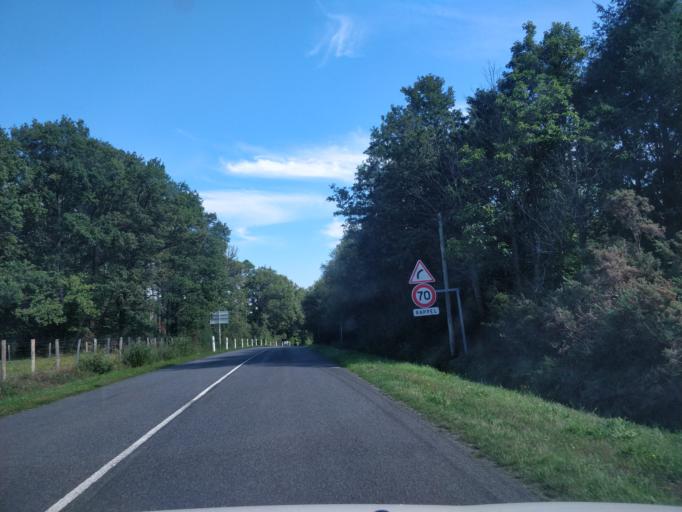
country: FR
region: Pays de la Loire
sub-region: Departement de la Loire-Atlantique
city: Quilly
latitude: 47.4813
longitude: -1.9147
